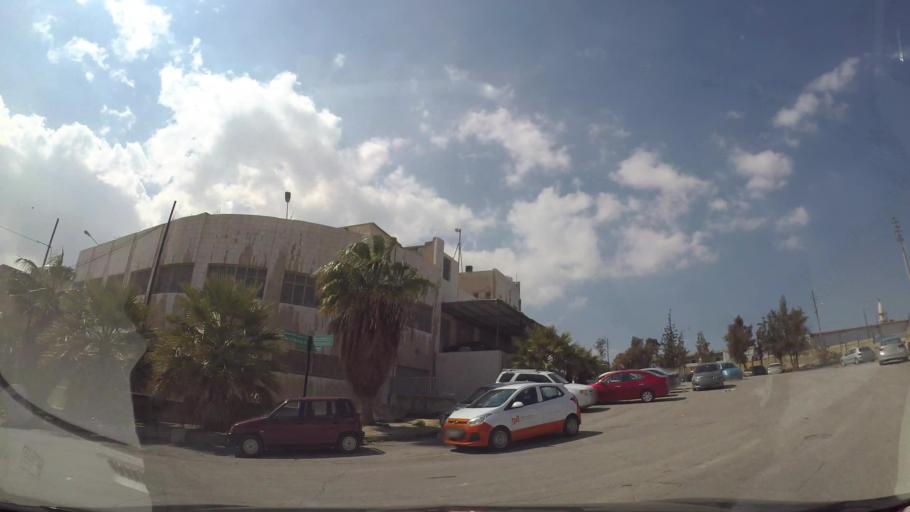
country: JO
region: Zarqa
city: Russeifa
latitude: 31.9906
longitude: 36.0049
